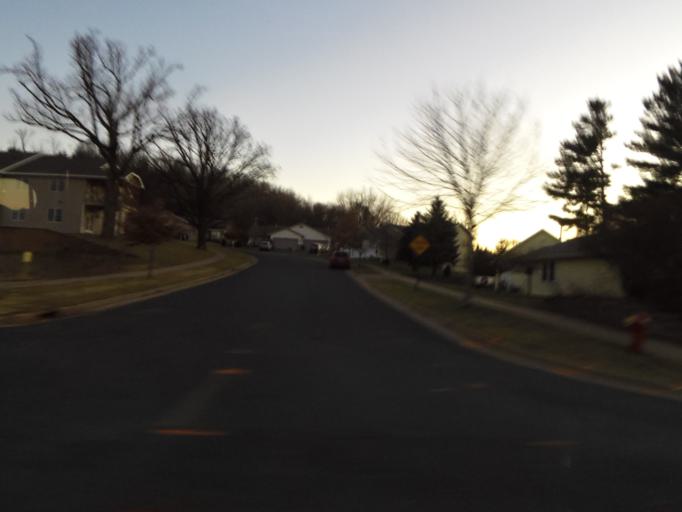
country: US
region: Wisconsin
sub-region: Pierce County
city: River Falls
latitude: 44.8626
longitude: -92.6088
